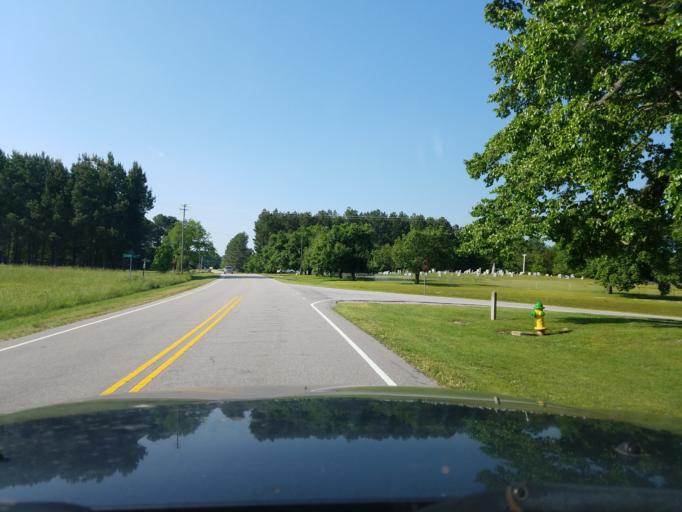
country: US
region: North Carolina
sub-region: Vance County
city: Henderson
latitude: 36.3894
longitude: -78.3678
